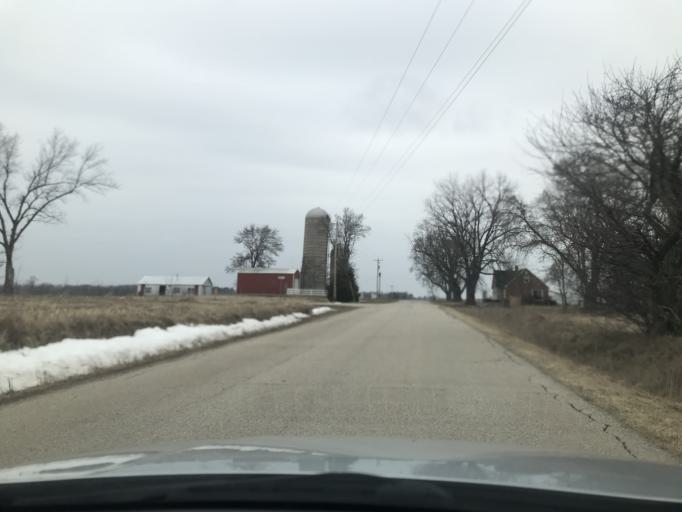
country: US
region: Wisconsin
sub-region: Marinette County
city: Peshtigo
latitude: 45.0554
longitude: -87.8509
